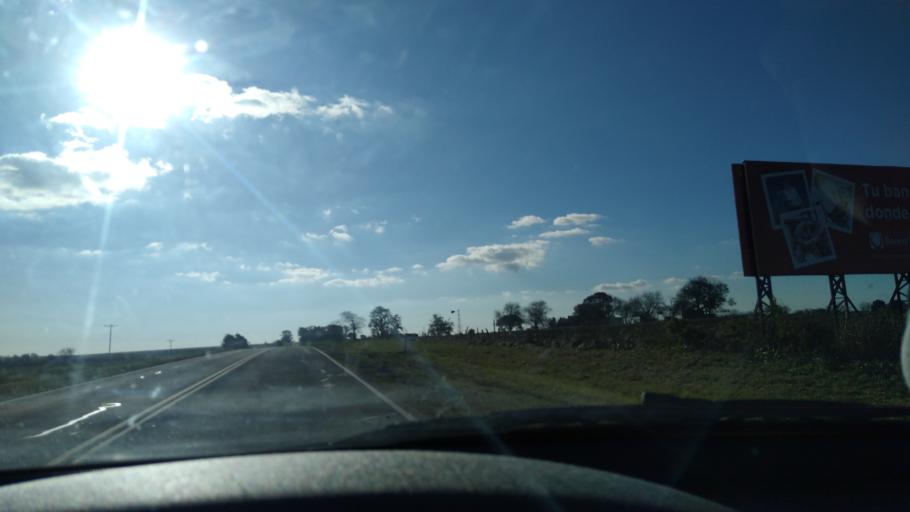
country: AR
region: Entre Rios
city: Diamante
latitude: -32.1082
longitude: -60.5791
